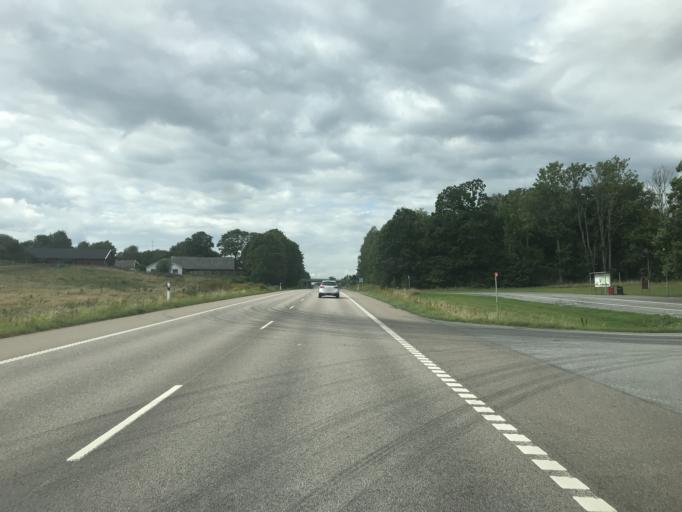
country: SE
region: Skane
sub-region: Hassleholms Kommun
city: Hassleholm
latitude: 56.1380
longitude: 13.8072
